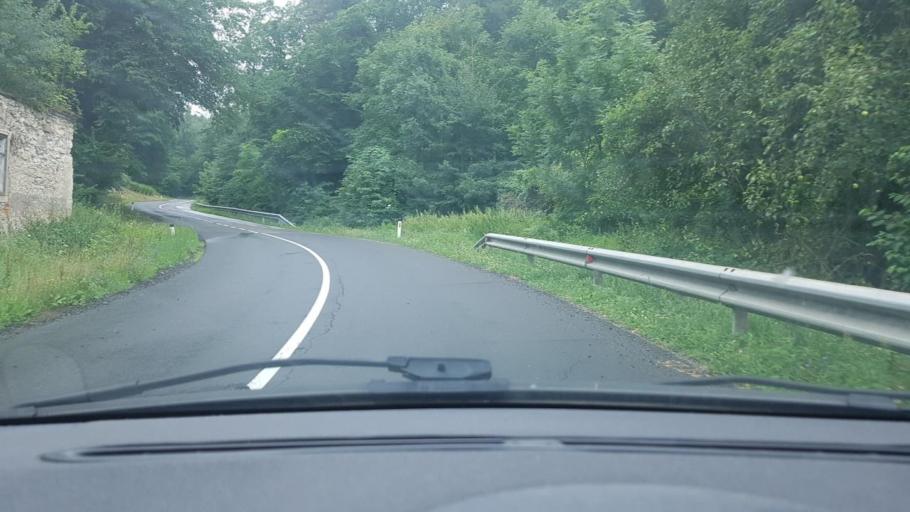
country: AT
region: Styria
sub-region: Politischer Bezirk Suedoststeiermark
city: Mureck
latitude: 46.7051
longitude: 15.7839
